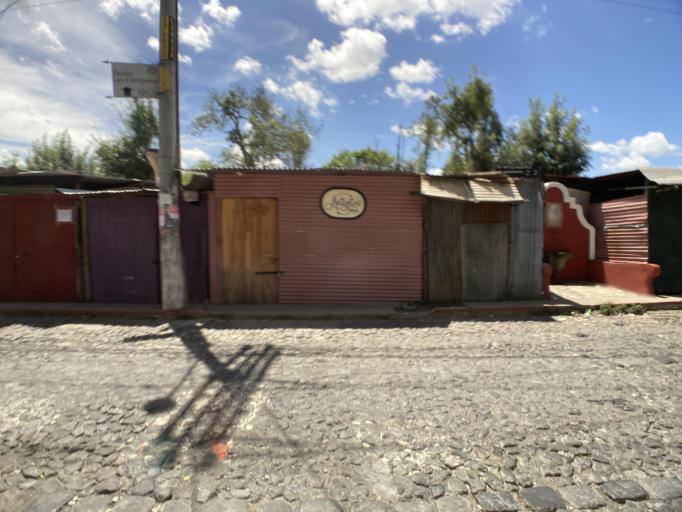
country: GT
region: Sacatepequez
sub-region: Municipio de Santa Maria de Jesus
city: Santa Maria de Jesus
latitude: 14.5333
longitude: -90.7353
